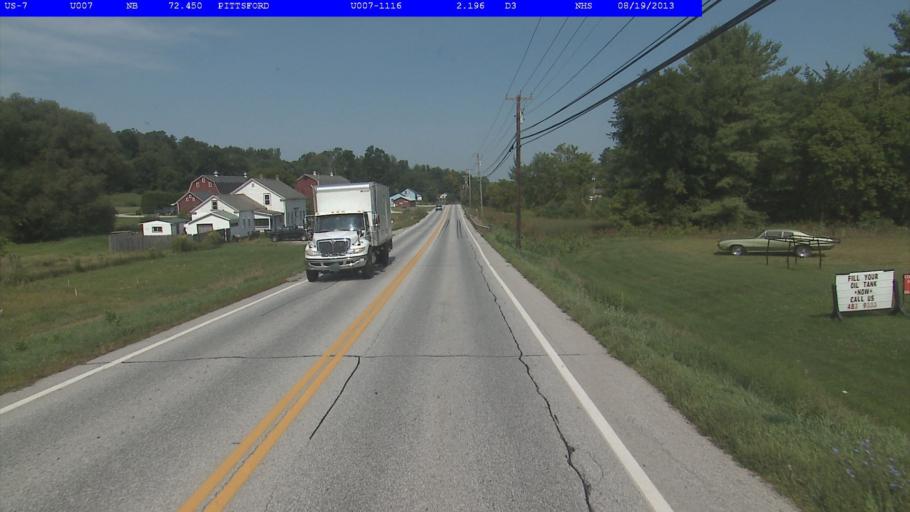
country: US
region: Vermont
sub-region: Rutland County
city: Rutland
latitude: 43.6940
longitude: -73.0017
